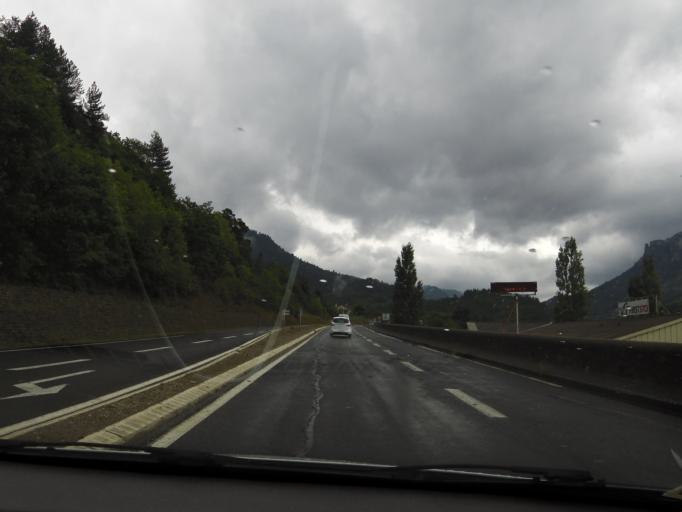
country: FR
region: Languedoc-Roussillon
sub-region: Departement de la Lozere
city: Florac
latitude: 44.3431
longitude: 3.5832
